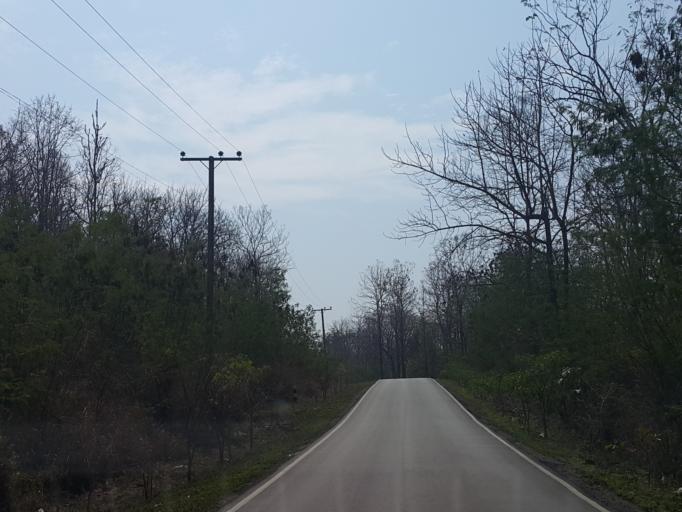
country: TH
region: Chiang Mai
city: Mae On
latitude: 18.8161
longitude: 99.2496
